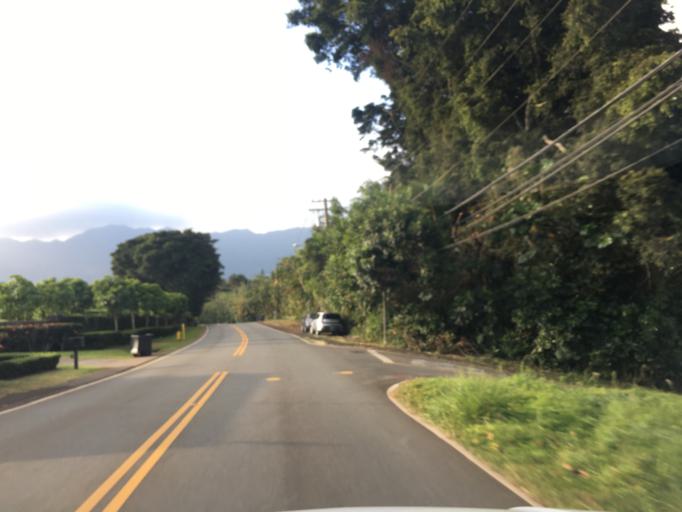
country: US
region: Hawaii
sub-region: Honolulu County
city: Maunawili
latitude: 21.3749
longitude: -157.7639
